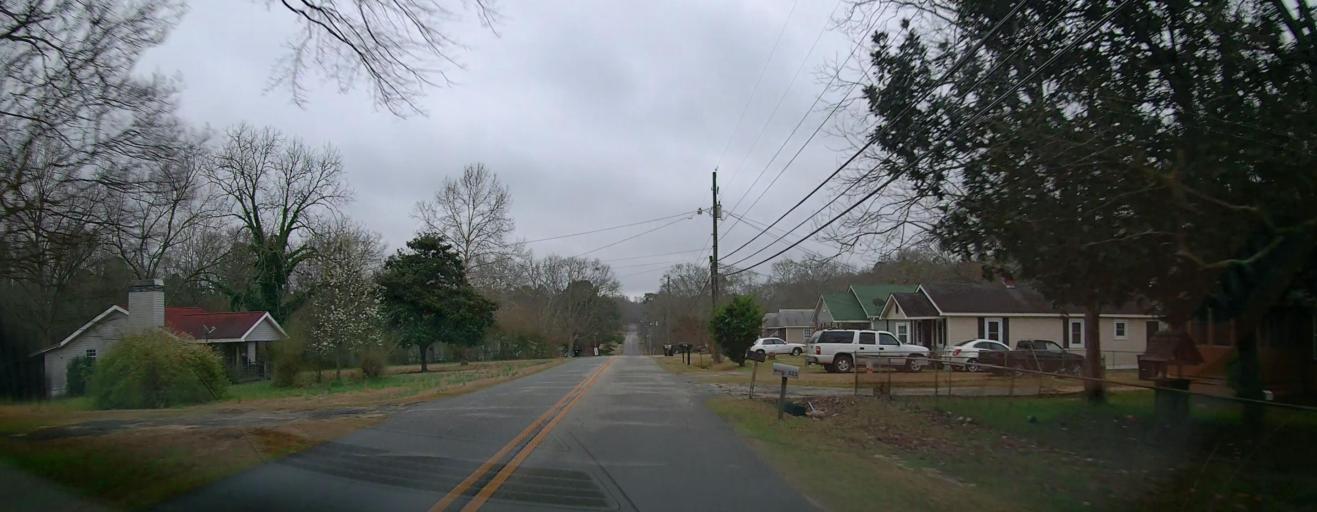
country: US
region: Georgia
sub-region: Lamar County
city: Barnesville
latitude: 33.0601
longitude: -84.1436
